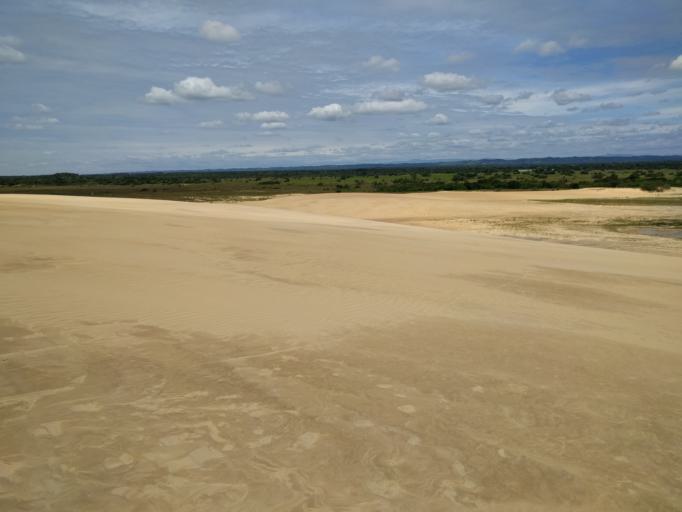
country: BO
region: Santa Cruz
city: Santa Cruz de la Sierra
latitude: -17.9416
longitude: -63.1602
